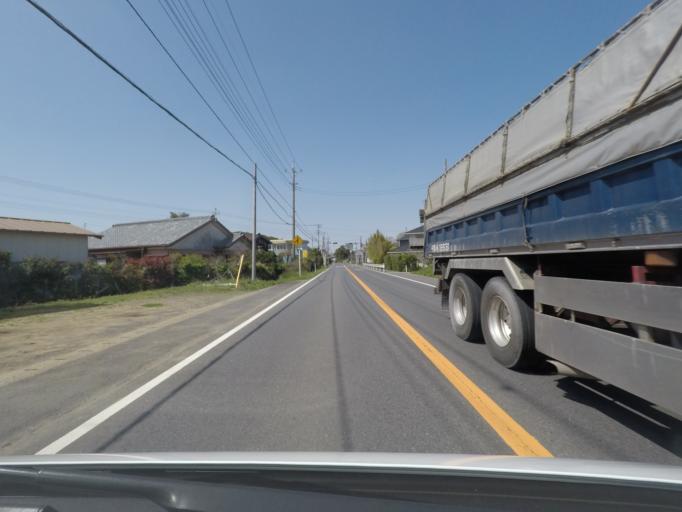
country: JP
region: Chiba
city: Omigawa
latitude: 35.8109
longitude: 140.7068
